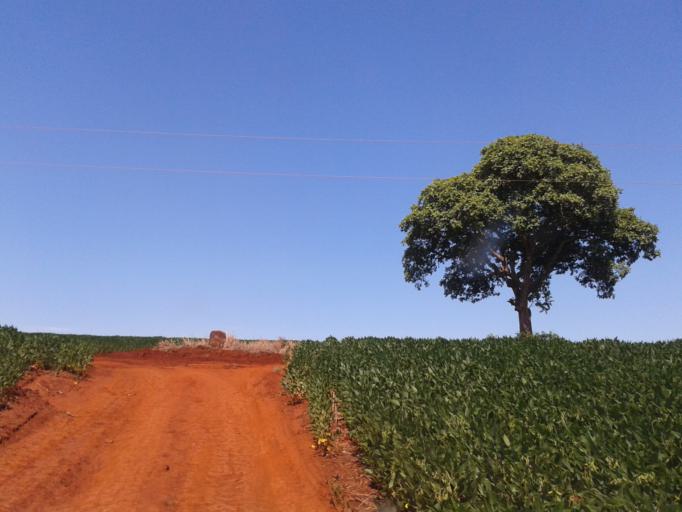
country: BR
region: Minas Gerais
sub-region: Centralina
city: Centralina
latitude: -18.6516
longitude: -49.2989
